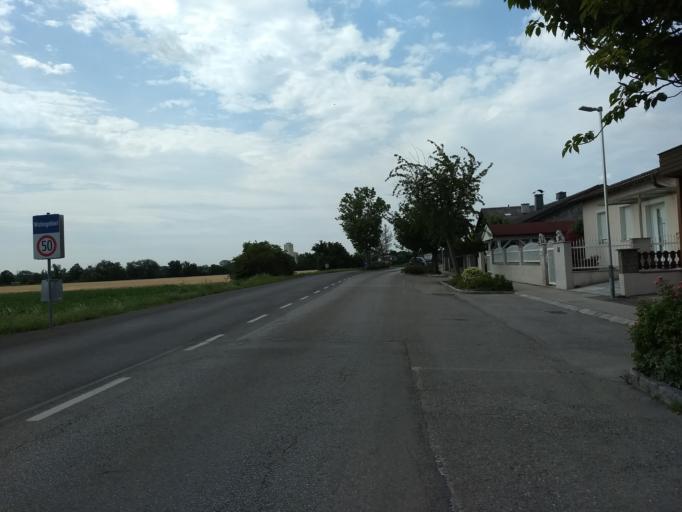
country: AT
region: Lower Austria
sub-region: Politischer Bezirk Modling
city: Neu-Guntramsdorf
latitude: 48.0555
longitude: 16.3231
